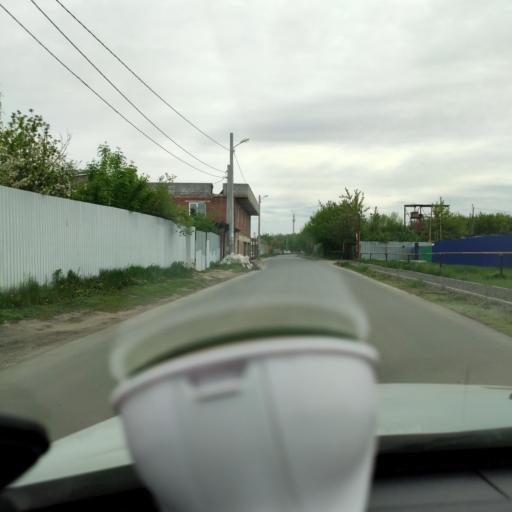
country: RU
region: Samara
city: Smyshlyayevka
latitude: 53.2133
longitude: 50.3276
